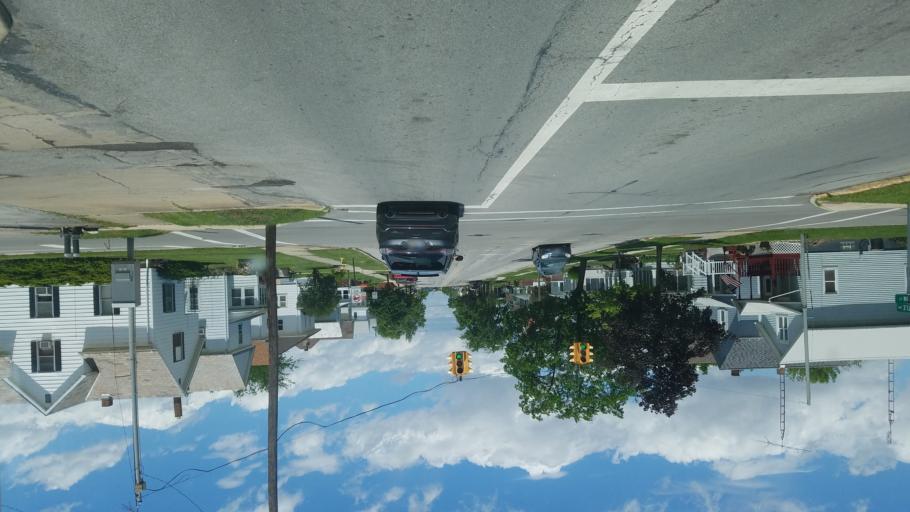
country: US
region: Ohio
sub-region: Huron County
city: Willard
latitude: 41.0529
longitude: -82.7260
